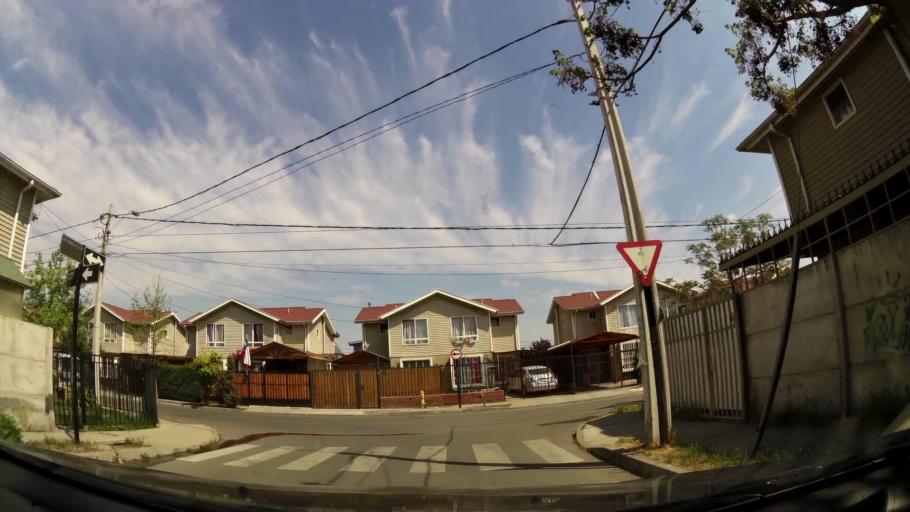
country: CL
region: Santiago Metropolitan
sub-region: Provincia de Cordillera
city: Puente Alto
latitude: -33.5804
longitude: -70.5849
